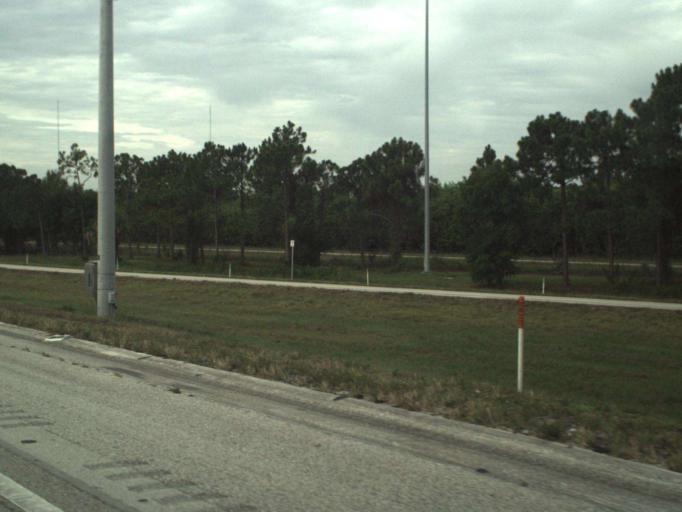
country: US
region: Florida
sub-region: Martin County
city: Palm City
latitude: 27.1593
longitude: -80.3898
